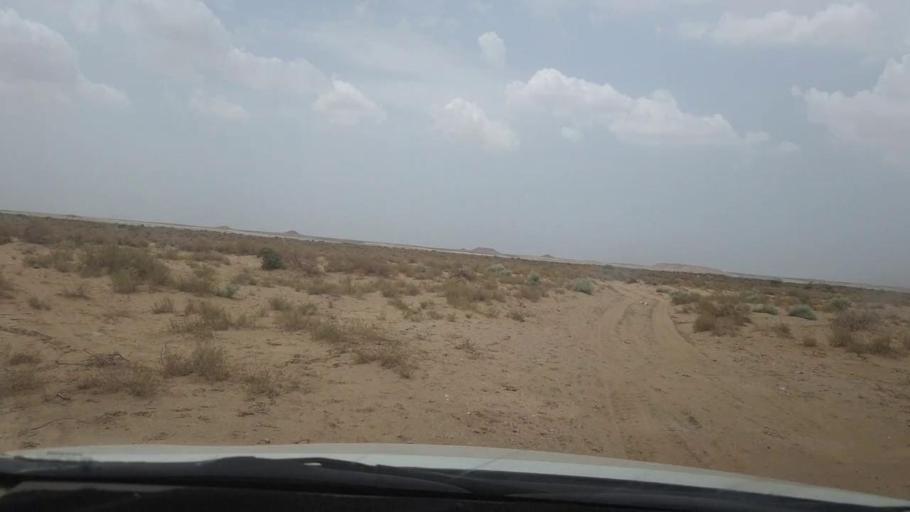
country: PK
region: Sindh
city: Khairpur
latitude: 27.4032
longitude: 68.9659
